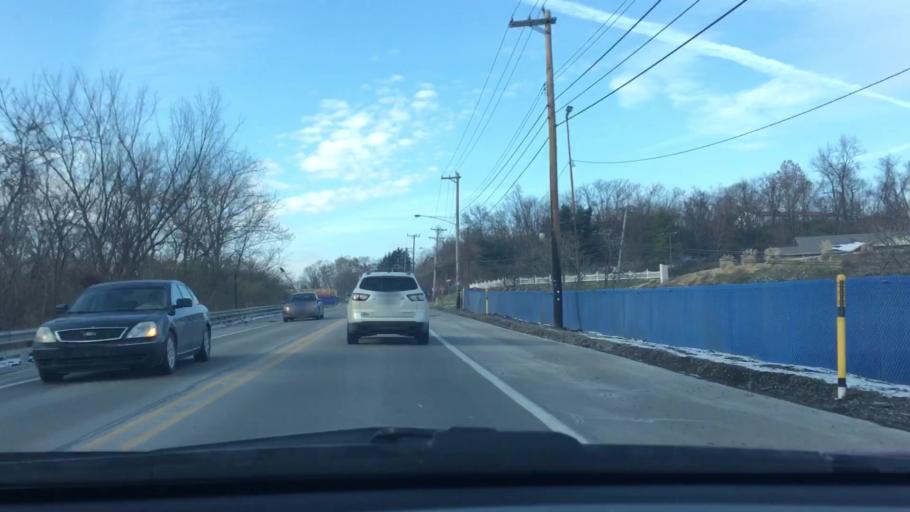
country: US
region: Pennsylvania
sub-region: Allegheny County
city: Glassport
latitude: 40.3399
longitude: -79.9142
